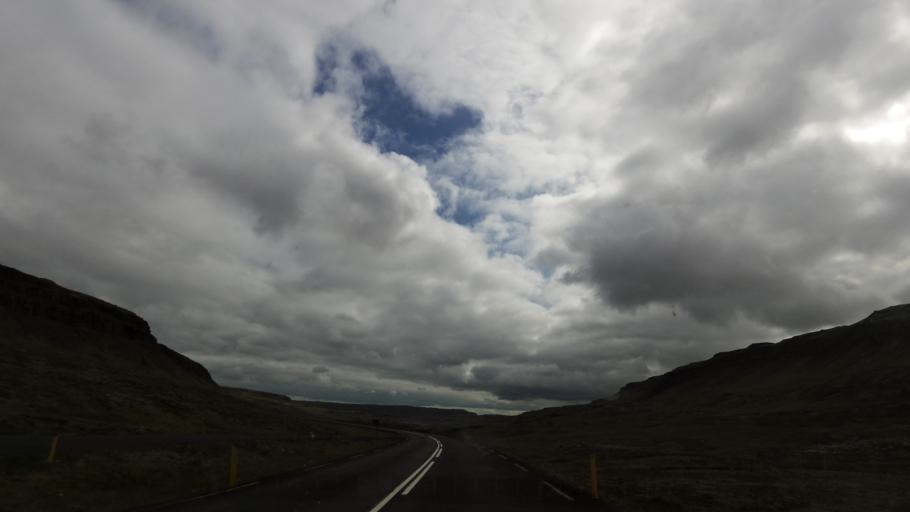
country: IS
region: West
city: Borgarnes
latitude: 64.8297
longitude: -21.4859
